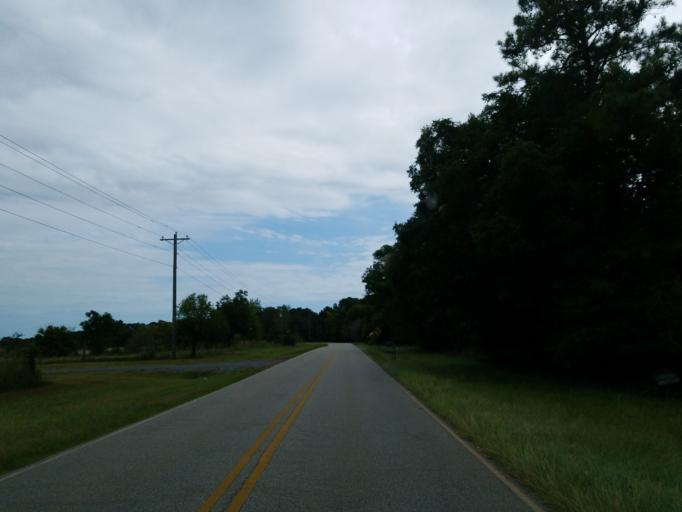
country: US
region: Georgia
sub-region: Monroe County
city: Forsyth
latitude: 32.9347
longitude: -83.9326
